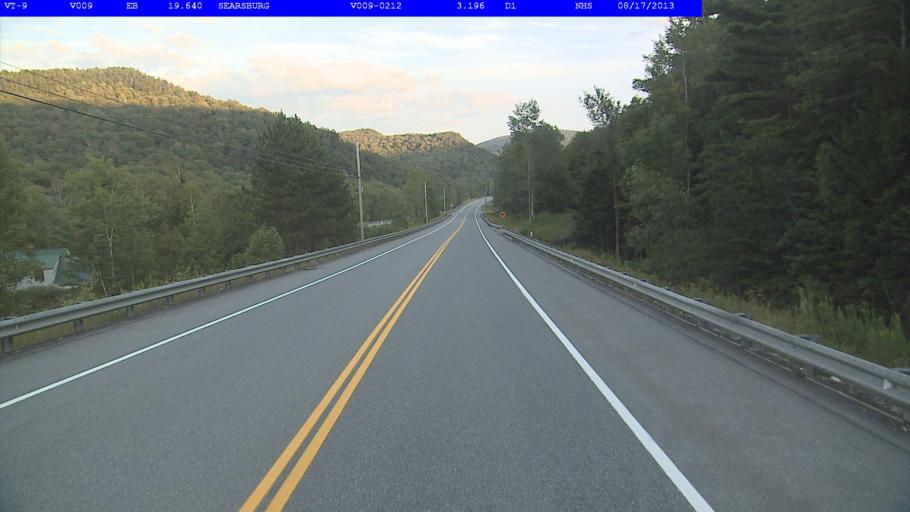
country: US
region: Vermont
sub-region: Windham County
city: Dover
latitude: 42.8915
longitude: -72.9539
